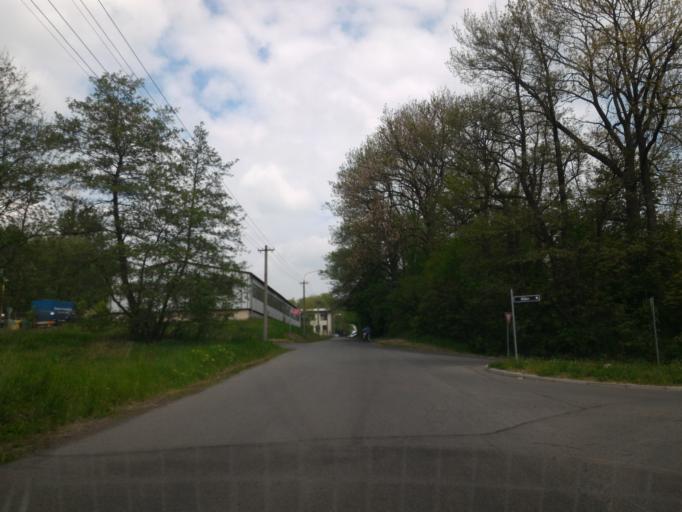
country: CZ
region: Ustecky
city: Varnsdorf
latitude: 50.9075
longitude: 14.6132
